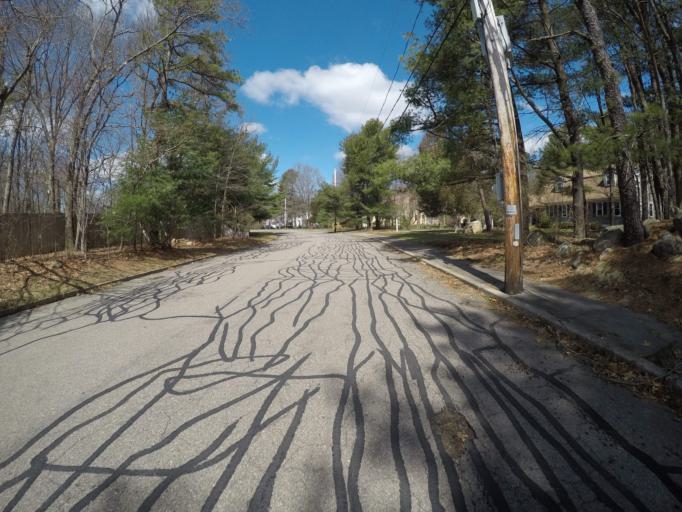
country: US
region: Massachusetts
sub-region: Bristol County
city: Easton
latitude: 42.0663
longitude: -71.1282
